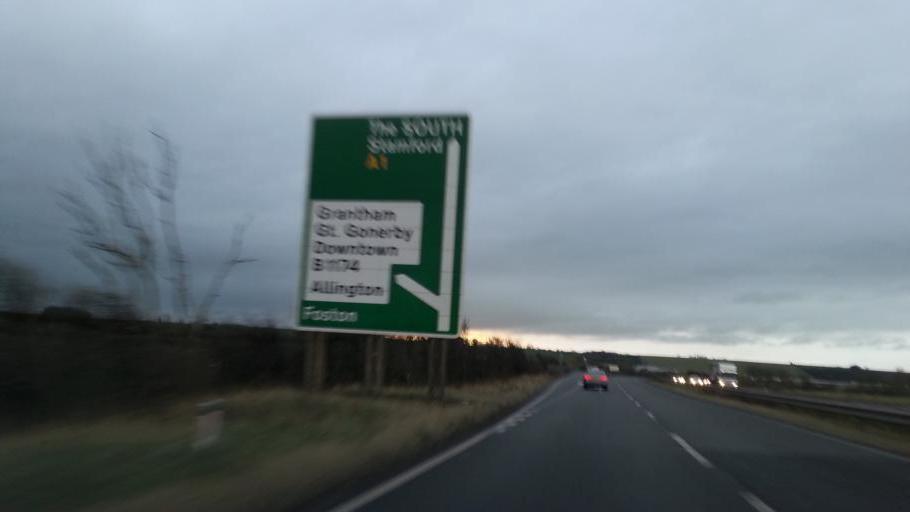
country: GB
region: England
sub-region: Lincolnshire
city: Great Gonerby
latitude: 52.9569
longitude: -0.6857
